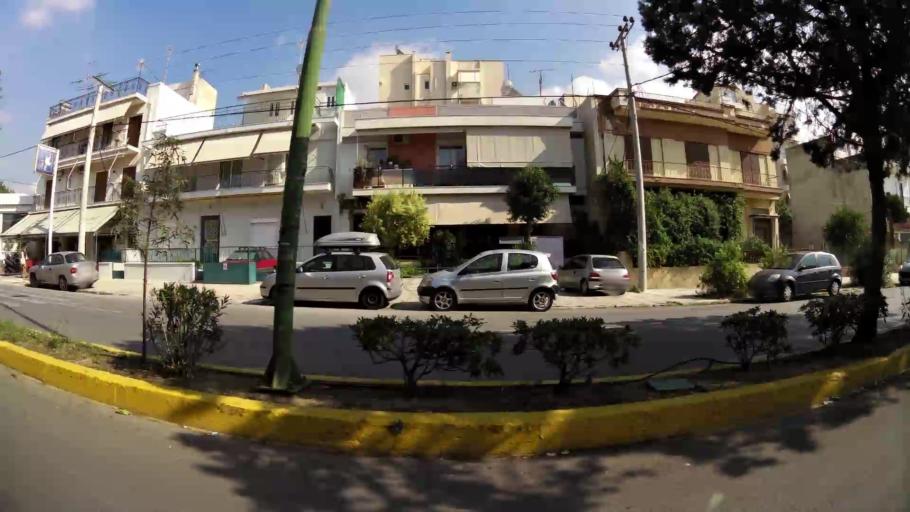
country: GR
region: Attica
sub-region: Nomarchia Athinas
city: Ilioupoli
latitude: 37.9295
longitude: 23.7514
